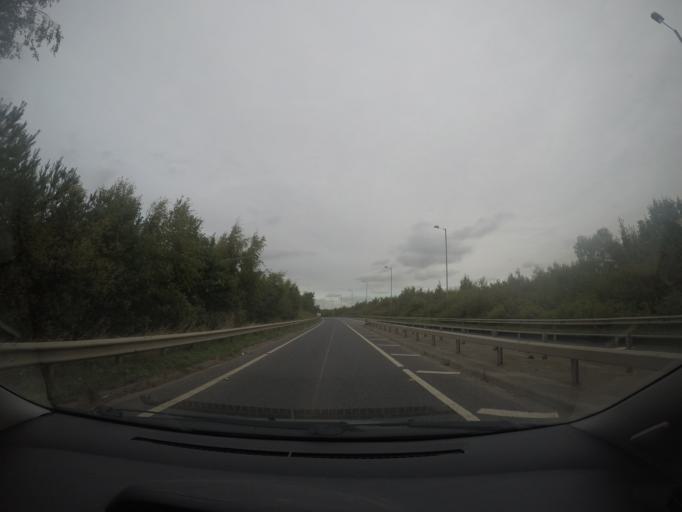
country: GB
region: England
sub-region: North Yorkshire
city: Barlby
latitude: 53.7782
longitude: -1.0372
